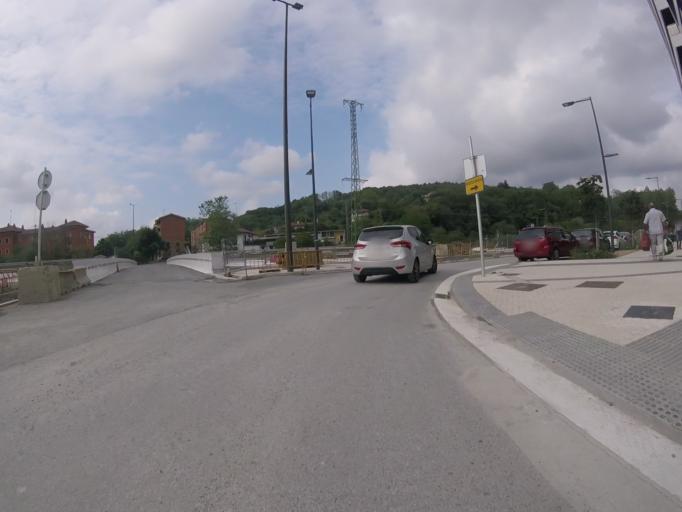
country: ES
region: Basque Country
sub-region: Provincia de Guipuzcoa
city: San Sebastian
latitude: 43.3053
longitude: -1.9619
